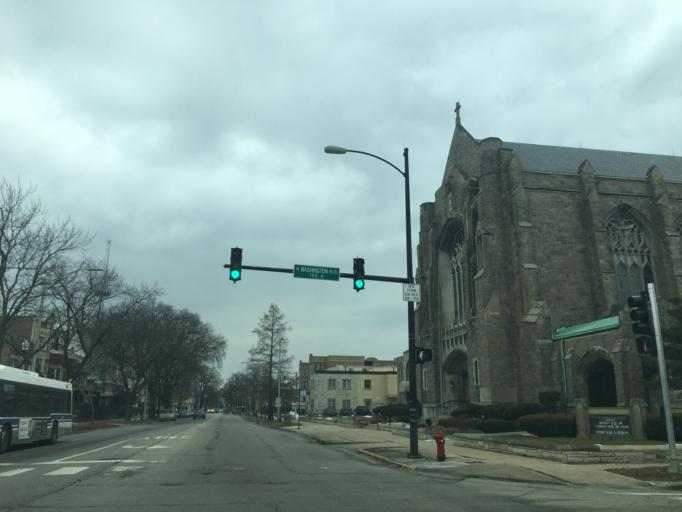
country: US
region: Illinois
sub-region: Cook County
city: Oak Park
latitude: 41.8821
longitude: -87.7748
